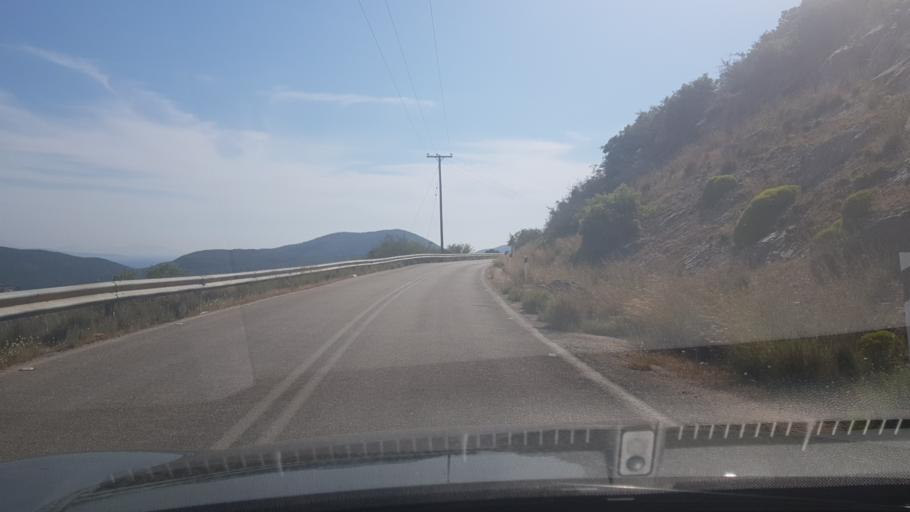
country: GR
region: Ionian Islands
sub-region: Lefkada
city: Nidri
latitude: 38.6505
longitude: 20.6634
